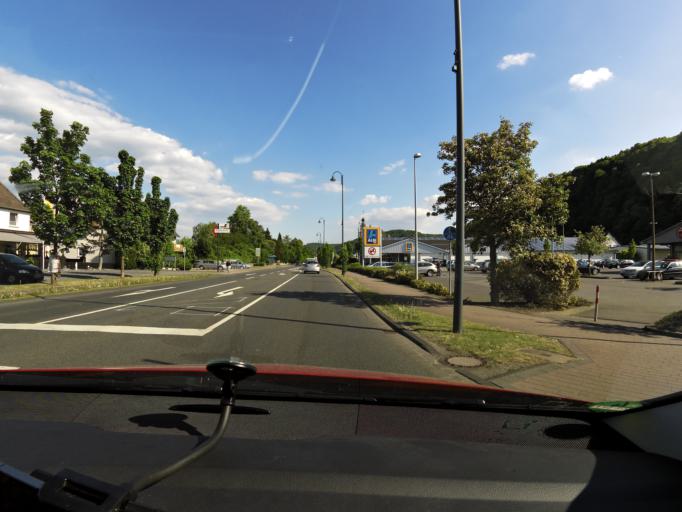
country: DE
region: Rheinland-Pfalz
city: Bad Breisig
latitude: 50.5163
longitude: 7.2921
